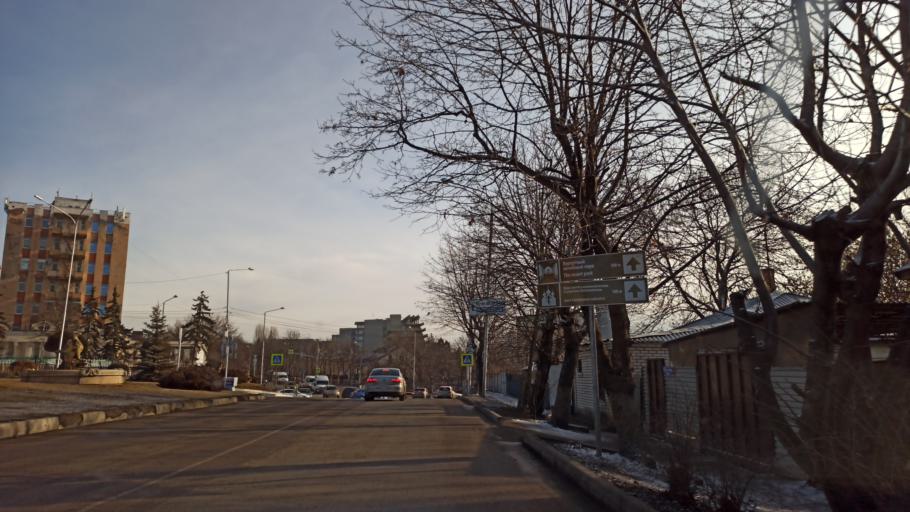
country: RU
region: Stavropol'skiy
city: Yessentuki
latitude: 44.0454
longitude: 42.8517
